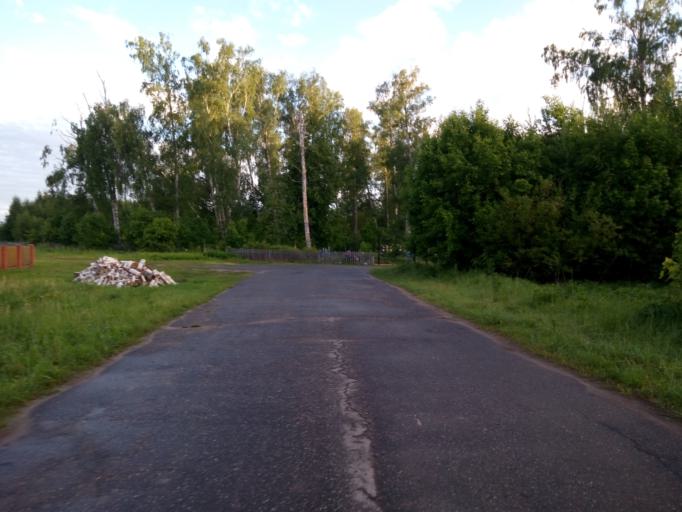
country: RU
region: Nizjnij Novgorod
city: Voskresenskoye
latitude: 56.7745
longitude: 45.5395
